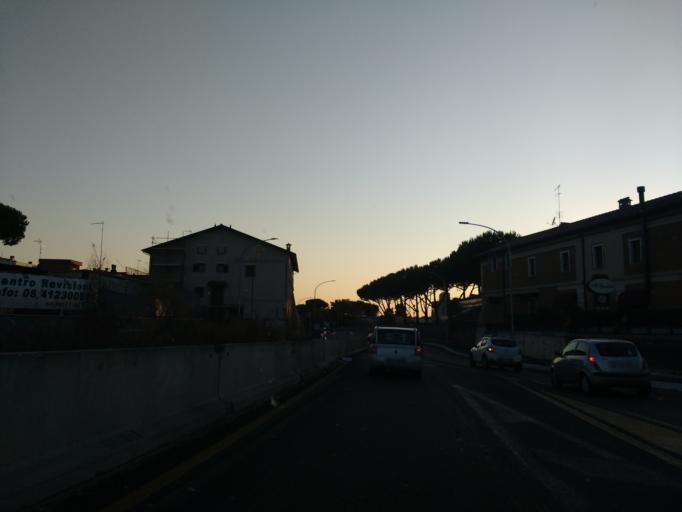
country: IT
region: Latium
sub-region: Citta metropolitana di Roma Capitale
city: Setteville
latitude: 41.9380
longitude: 12.6213
